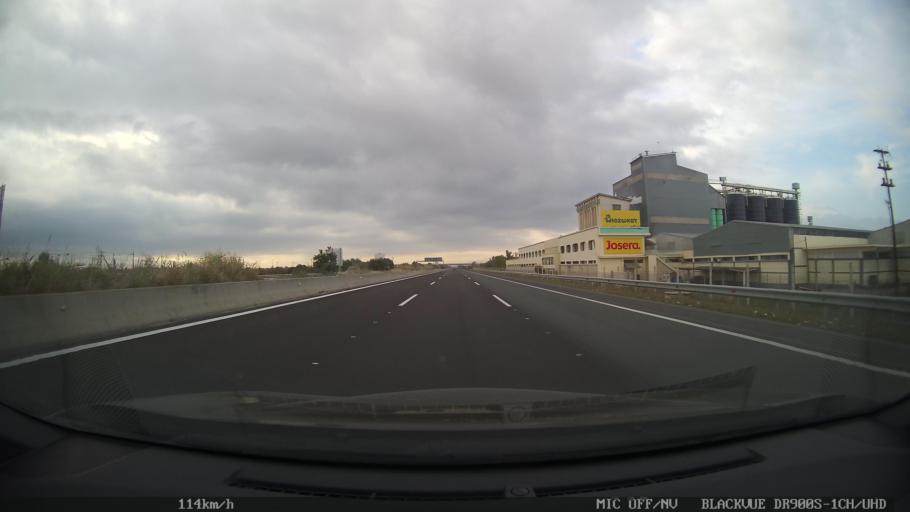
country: GR
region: Central Macedonia
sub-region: Nomos Pierias
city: Peristasi
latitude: 40.2488
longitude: 22.5335
